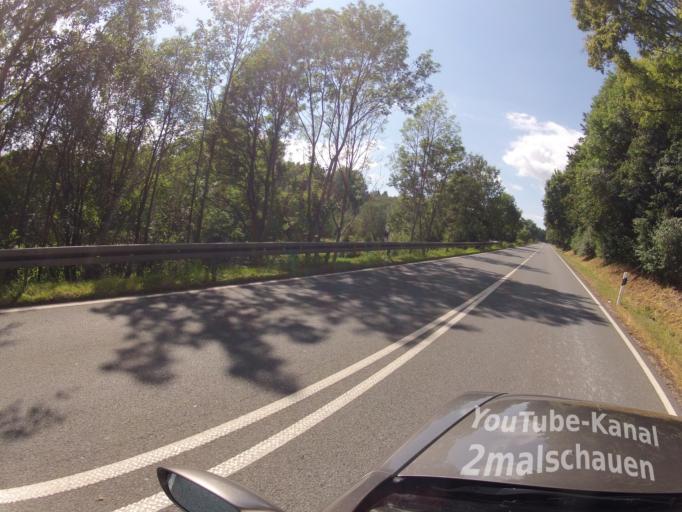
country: DE
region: Bavaria
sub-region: Upper Franconia
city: Wunsiedel
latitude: 50.0444
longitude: 11.9942
